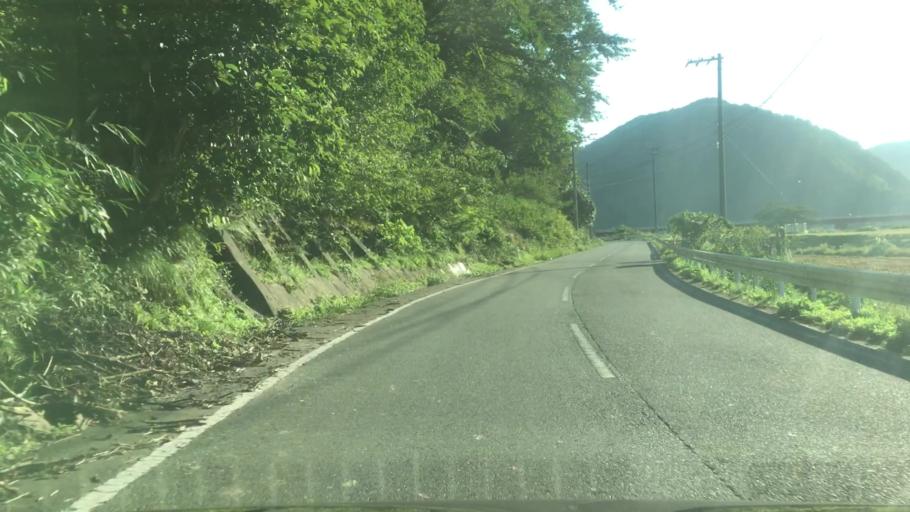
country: JP
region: Hyogo
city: Toyooka
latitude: 35.6092
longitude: 134.8084
